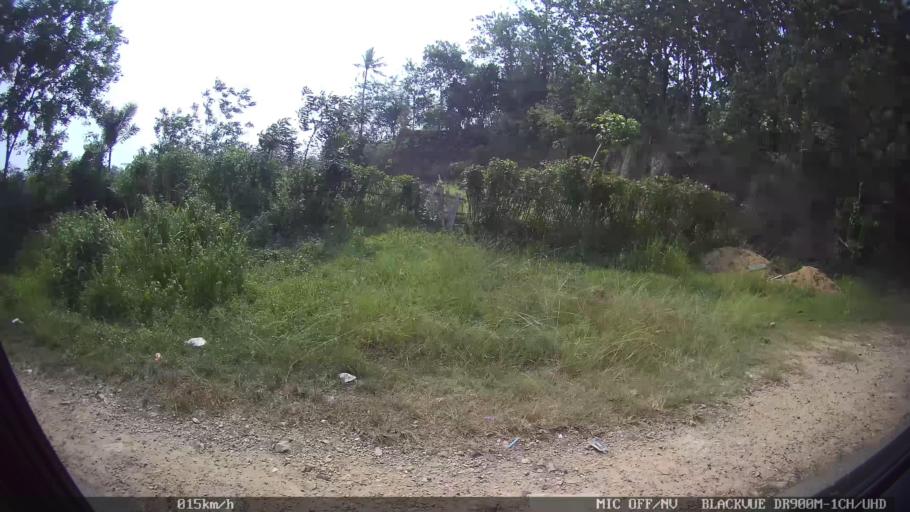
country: ID
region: Lampung
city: Pringsewu
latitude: -5.4043
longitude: 104.9926
